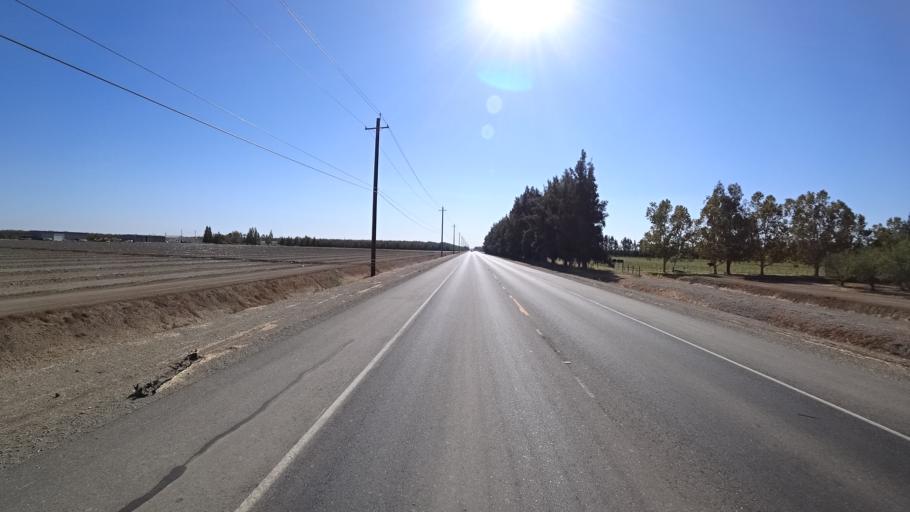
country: US
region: California
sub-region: Yolo County
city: Woodland
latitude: 38.6079
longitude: -121.8030
